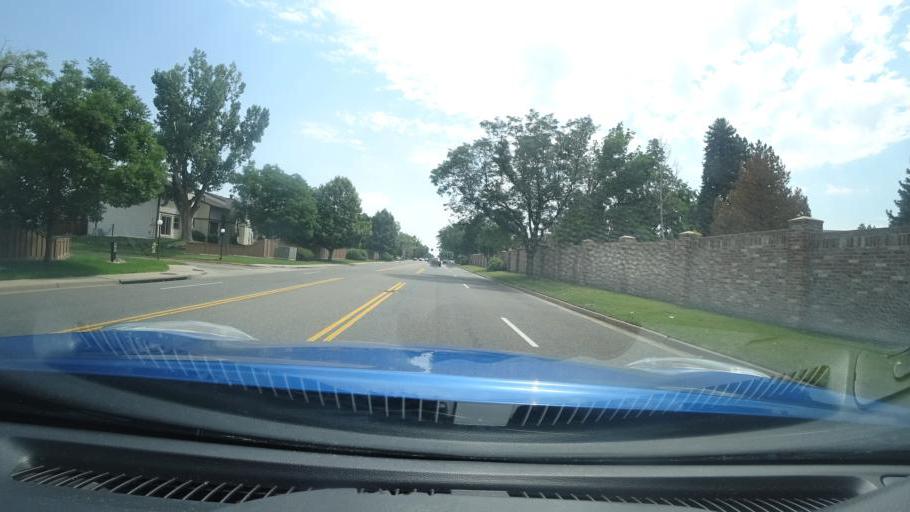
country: US
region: Colorado
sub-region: Adams County
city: Aurora
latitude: 39.6675
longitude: -104.8494
